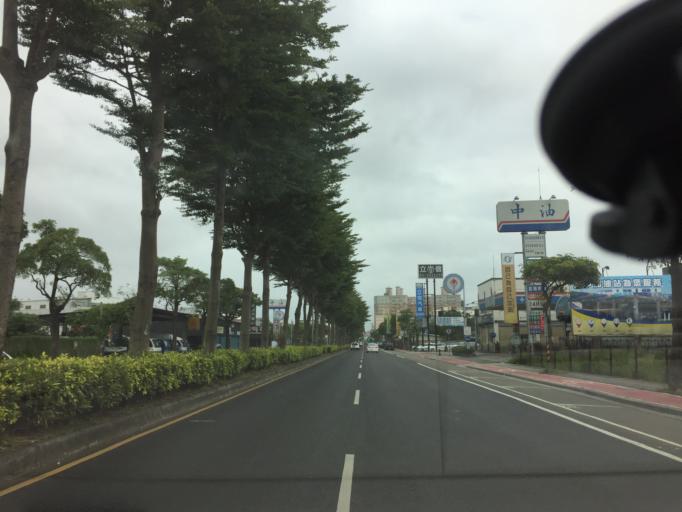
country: TW
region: Taiwan
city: Taoyuan City
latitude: 24.9918
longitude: 121.2695
